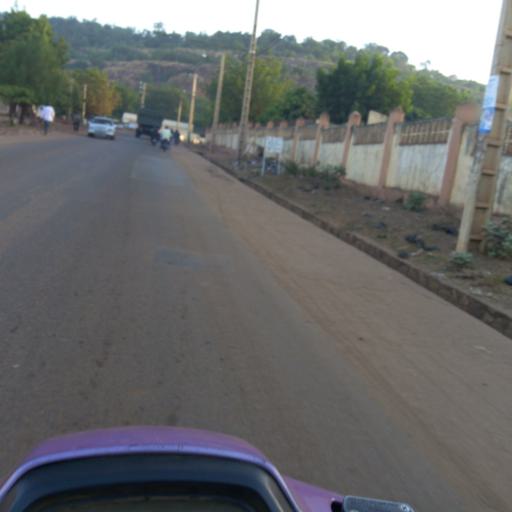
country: ML
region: Bamako
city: Bamako
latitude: 12.6555
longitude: -8.0116
